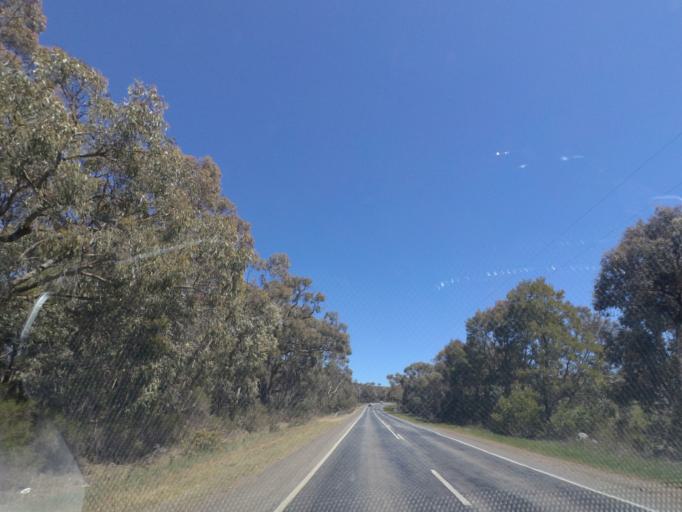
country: AU
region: Victoria
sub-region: Hume
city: Sunbury
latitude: -37.2989
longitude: 144.8170
